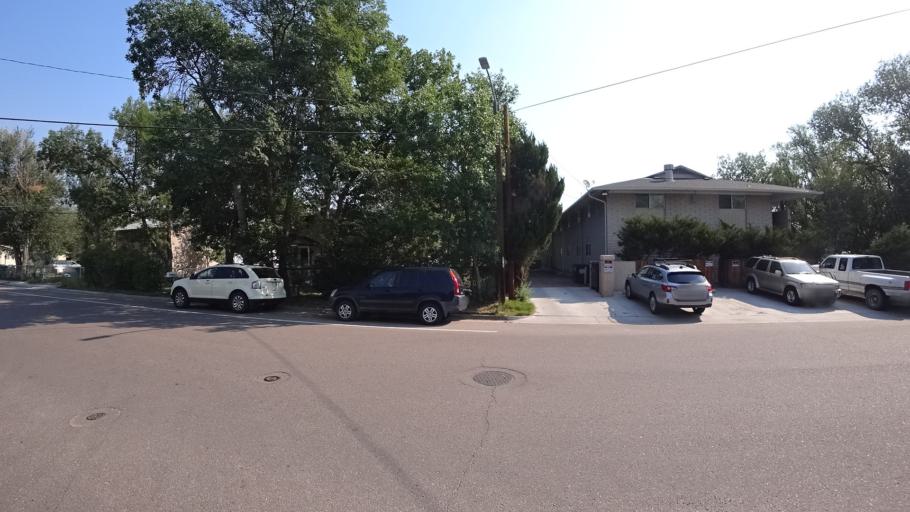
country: US
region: Colorado
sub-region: El Paso County
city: Colorado Springs
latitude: 38.8080
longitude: -104.8341
